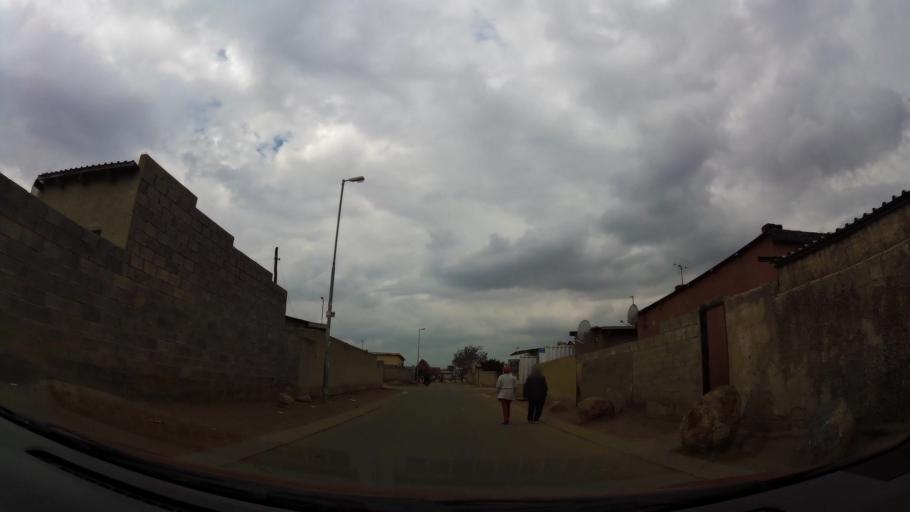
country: ZA
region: Gauteng
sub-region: City of Johannesburg Metropolitan Municipality
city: Soweto
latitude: -26.2523
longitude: 27.8500
